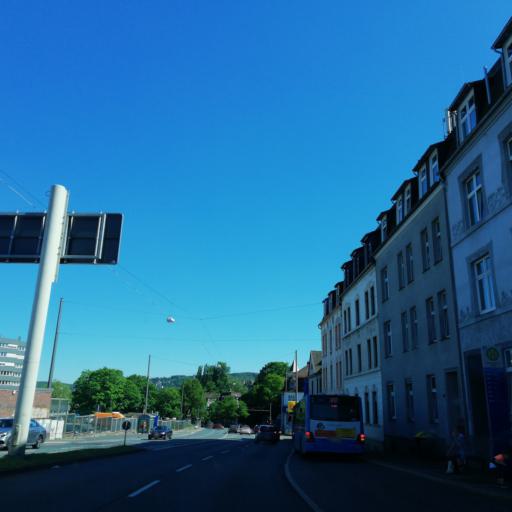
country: DE
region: North Rhine-Westphalia
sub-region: Regierungsbezirk Dusseldorf
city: Wuppertal
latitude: 51.2782
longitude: 7.1845
